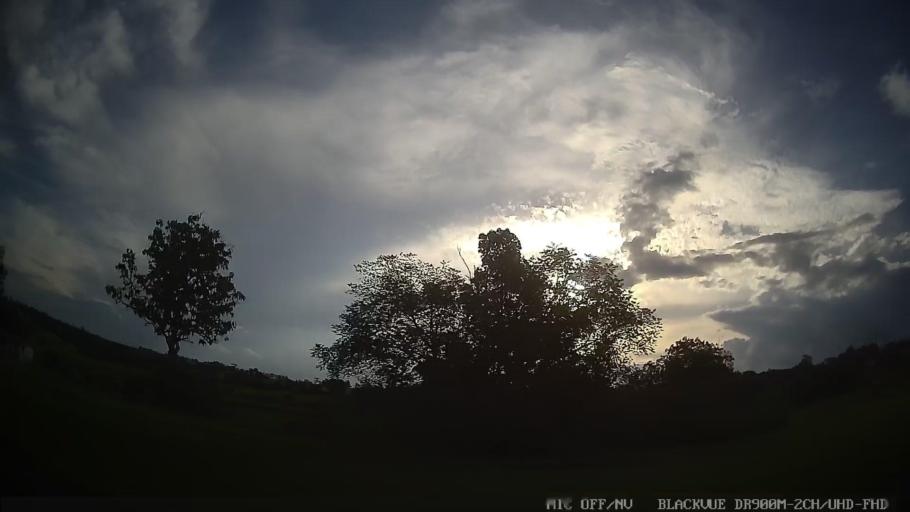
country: BR
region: Sao Paulo
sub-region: Tiete
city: Tiete
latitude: -23.1351
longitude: -47.6855
